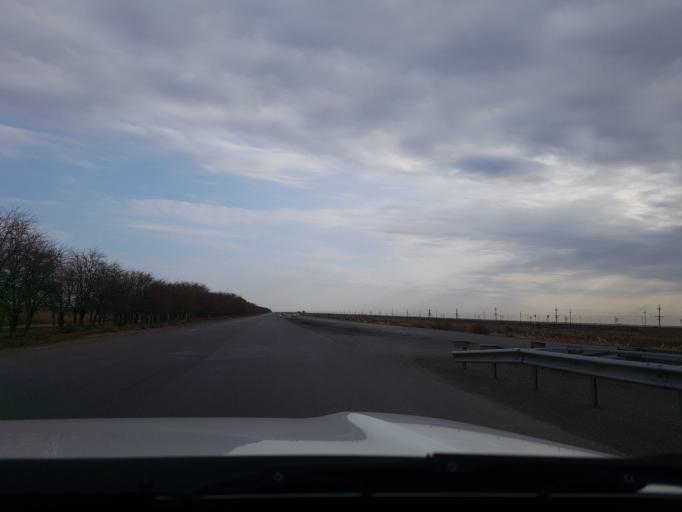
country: TM
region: Ahal
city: Tejen
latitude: 37.2392
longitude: 60.1687
